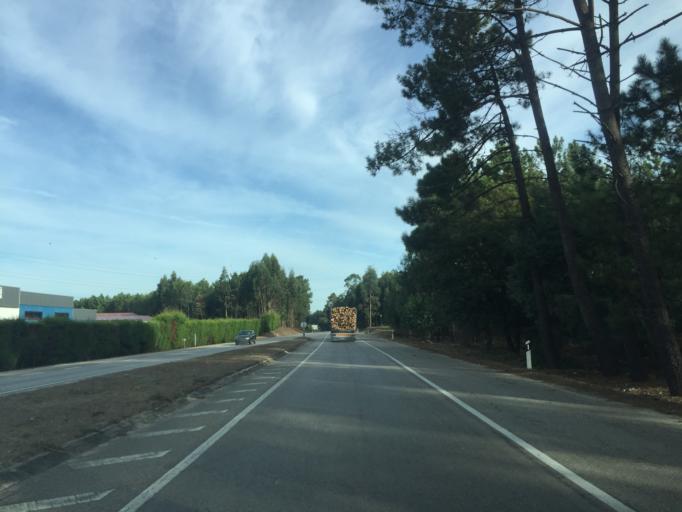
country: PT
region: Leiria
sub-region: Pombal
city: Lourical
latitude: 40.0097
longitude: -8.8067
